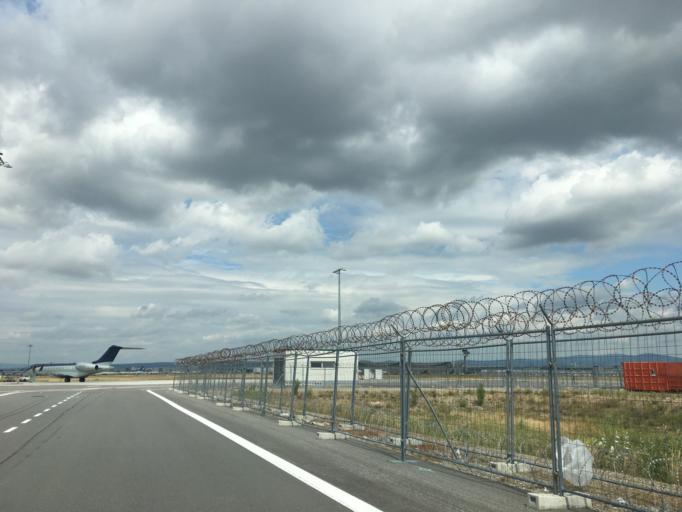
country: DE
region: Hesse
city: Morfelden-Walldorf
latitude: 50.0315
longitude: 8.5719
